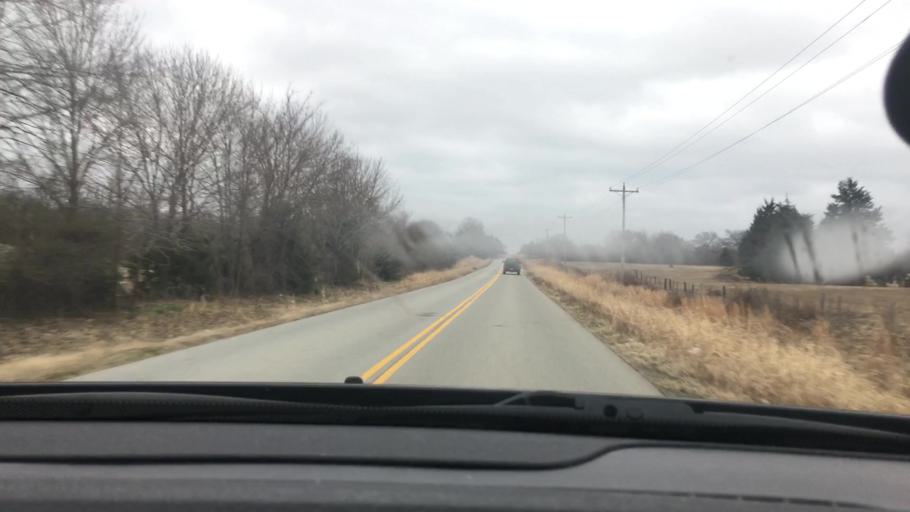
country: US
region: Oklahoma
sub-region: Atoka County
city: Atoka
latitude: 34.3214
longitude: -96.0755
